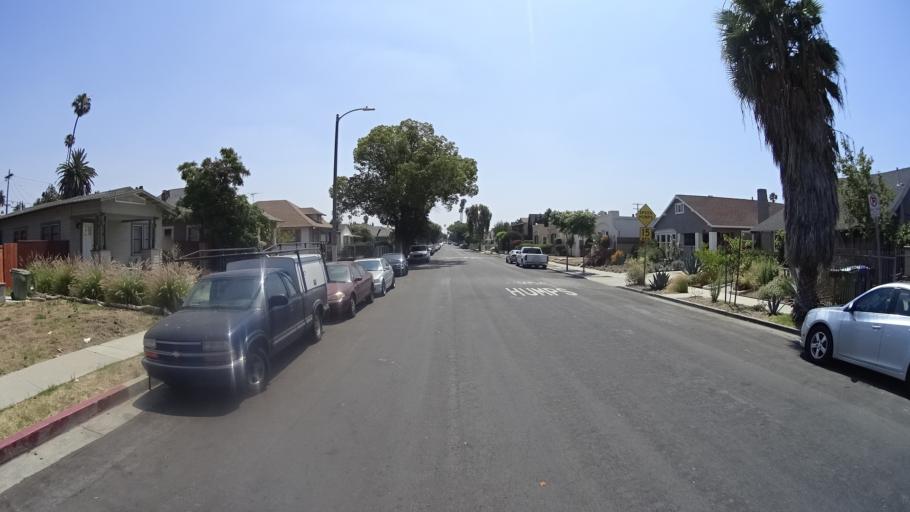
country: US
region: California
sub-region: Los Angeles County
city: View Park-Windsor Hills
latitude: 34.0299
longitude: -118.3175
